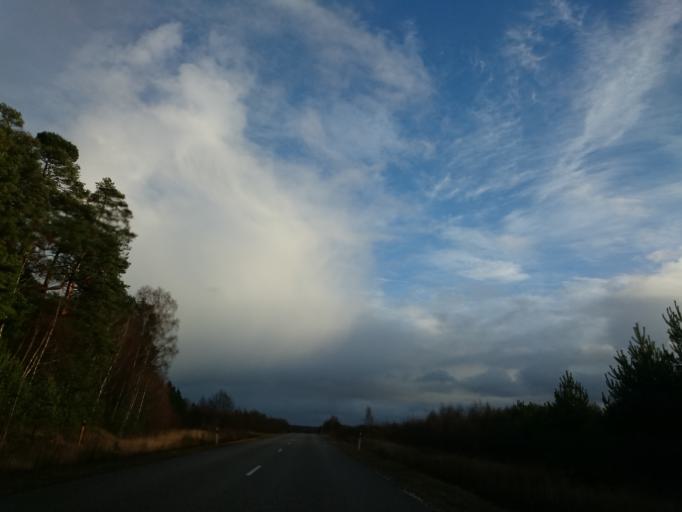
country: LV
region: Skrunda
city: Skrunda
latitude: 56.6771
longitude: 21.9615
